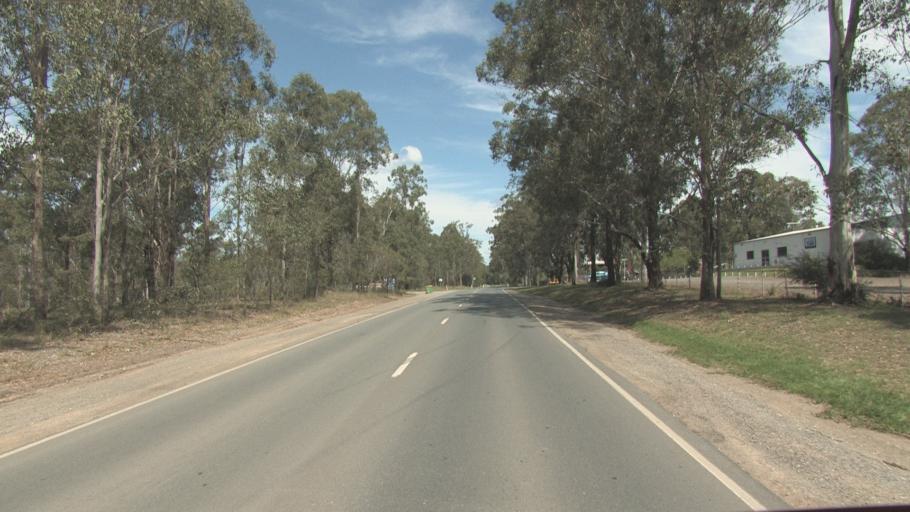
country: AU
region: Queensland
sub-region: Logan
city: North Maclean
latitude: -27.8246
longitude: 153.0331
